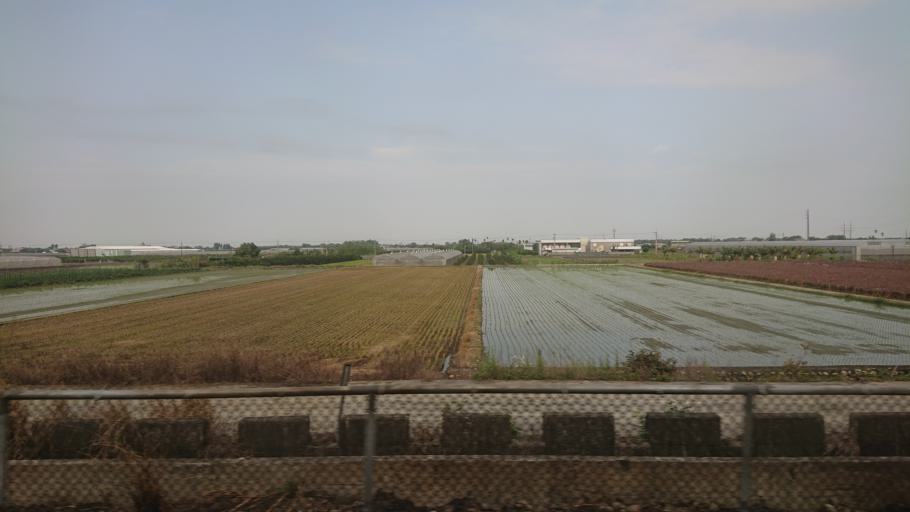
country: TW
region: Taiwan
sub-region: Yunlin
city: Douliu
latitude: 23.7345
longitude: 120.5826
